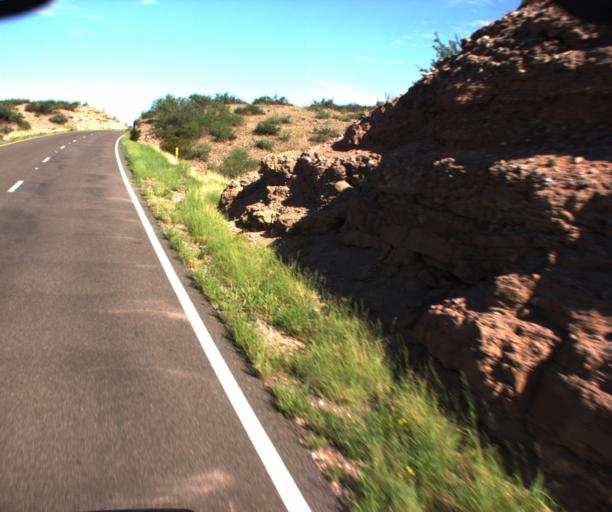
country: US
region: Arizona
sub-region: Greenlee County
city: Clifton
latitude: 32.9834
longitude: -109.2609
